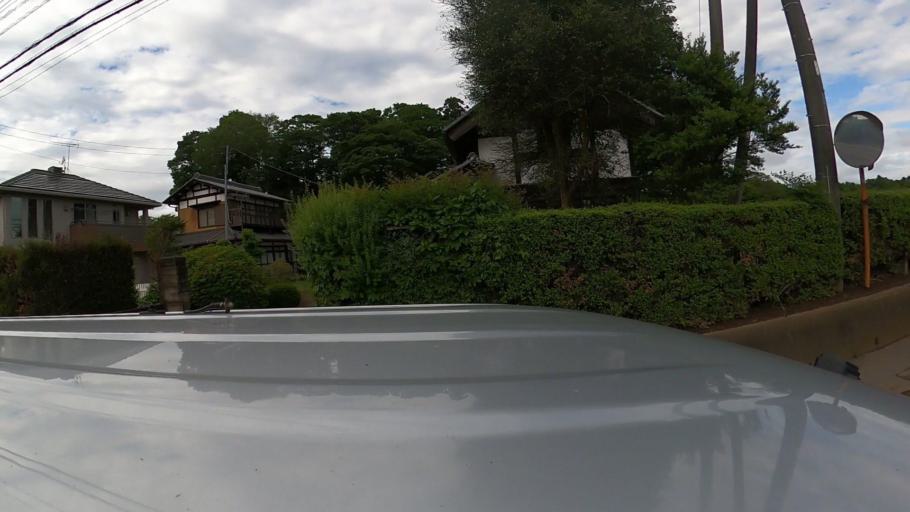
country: JP
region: Ibaraki
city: Ushiku
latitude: 35.9739
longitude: 140.1839
